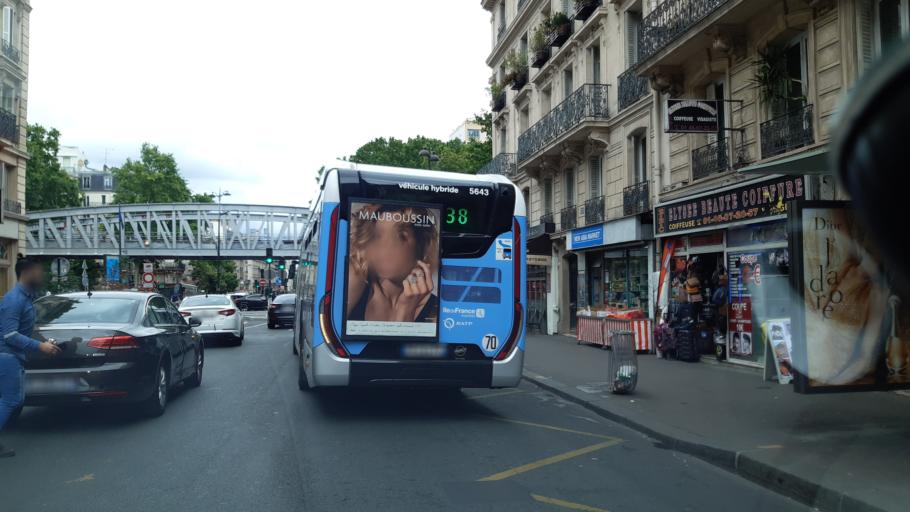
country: FR
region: Ile-de-France
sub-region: Paris
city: Saint-Ouen
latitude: 48.8837
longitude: 2.3593
